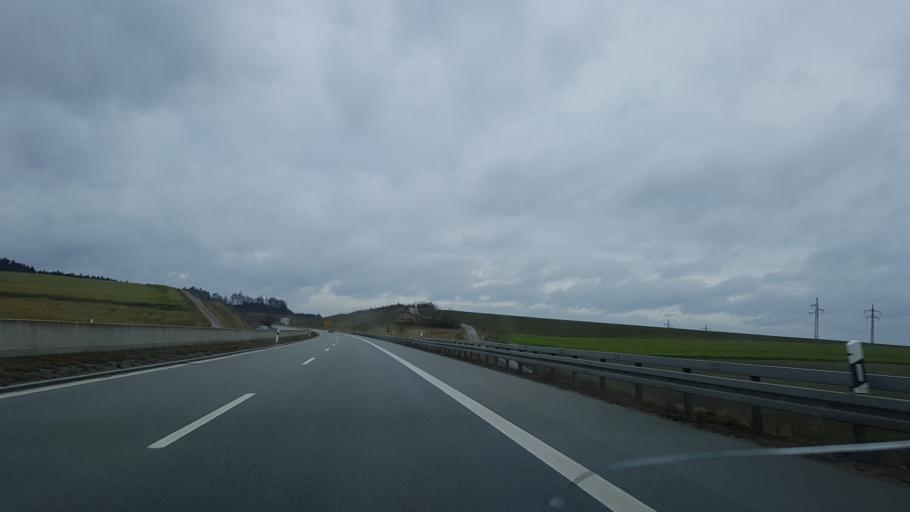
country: DE
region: Bavaria
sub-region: Lower Bavaria
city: Ergoldsbach
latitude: 48.7016
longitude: 12.1784
